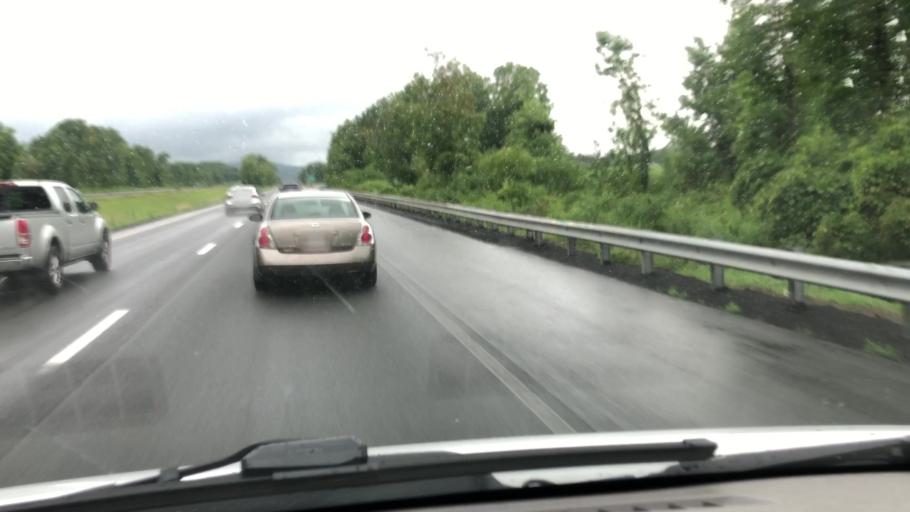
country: US
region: Massachusetts
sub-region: Franklin County
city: South Deerfield
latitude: 42.4999
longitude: -72.6181
